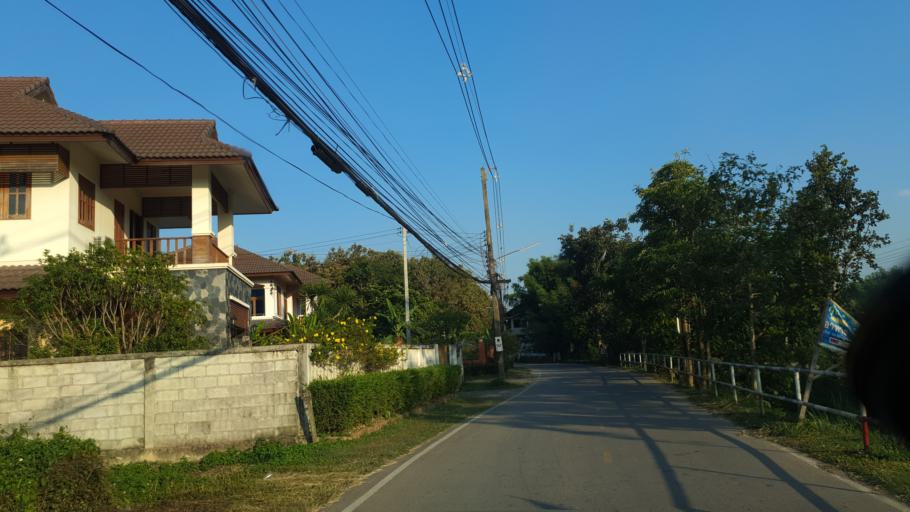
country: TH
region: Chiang Mai
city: San Sai
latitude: 18.9046
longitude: 98.9433
